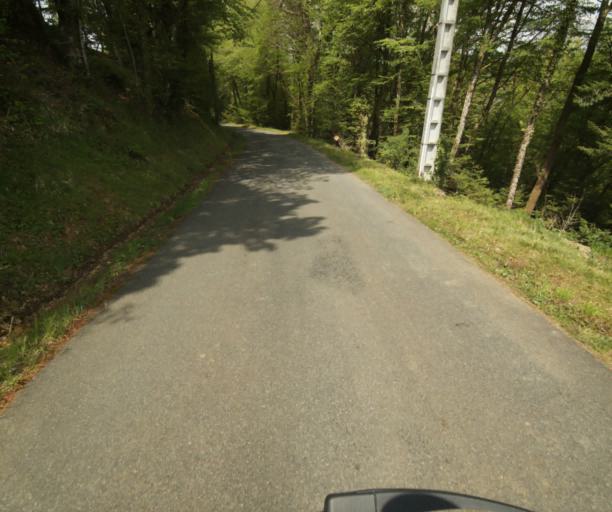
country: FR
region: Limousin
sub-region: Departement de la Correze
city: Tulle
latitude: 45.2772
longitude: 1.7579
